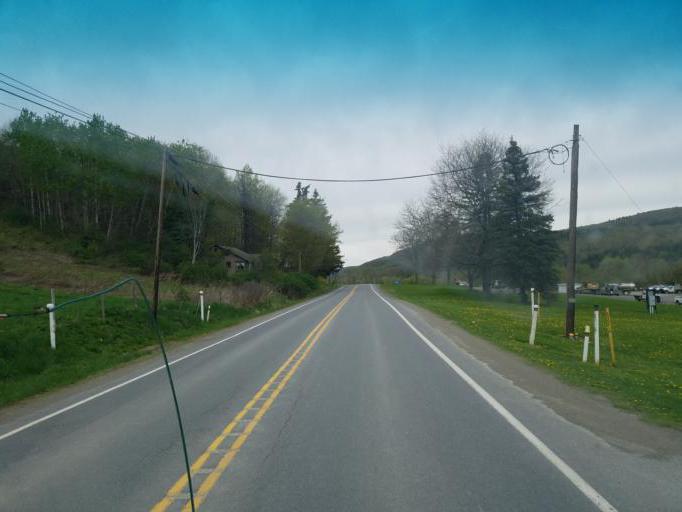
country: US
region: Pennsylvania
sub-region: Tioga County
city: Westfield
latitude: 41.8749
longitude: -77.5227
